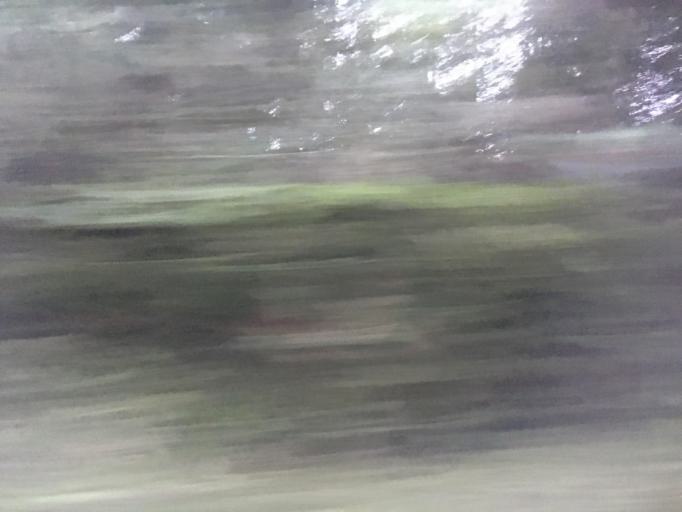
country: TW
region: Taiwan
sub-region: Yilan
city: Yilan
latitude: 24.5105
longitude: 121.5936
